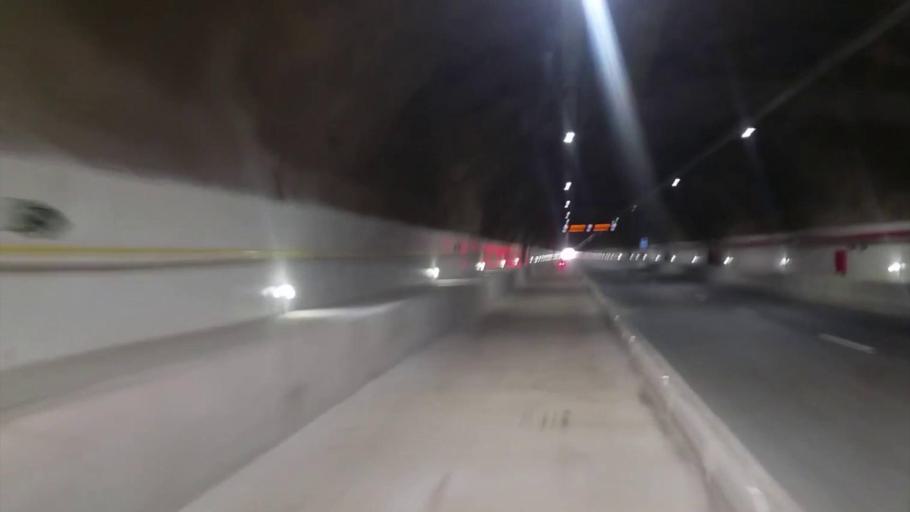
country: BR
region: Rio de Janeiro
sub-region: Nilopolis
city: Nilopolis
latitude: -22.8944
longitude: -43.3997
